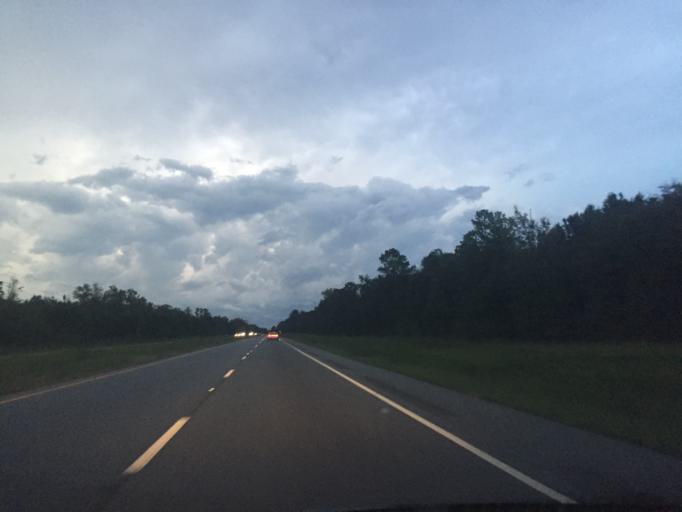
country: US
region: Georgia
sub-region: Liberty County
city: Midway
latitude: 31.8336
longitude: -81.4848
